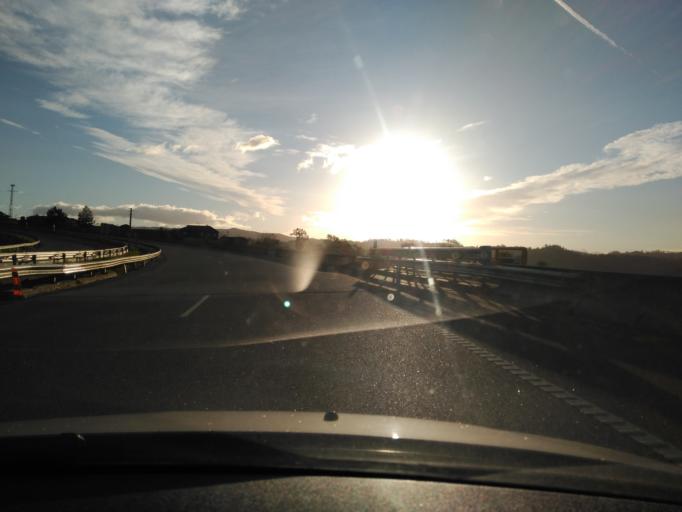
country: PT
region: Braga
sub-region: Fafe
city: Aroes
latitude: 41.4510
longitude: -8.2160
